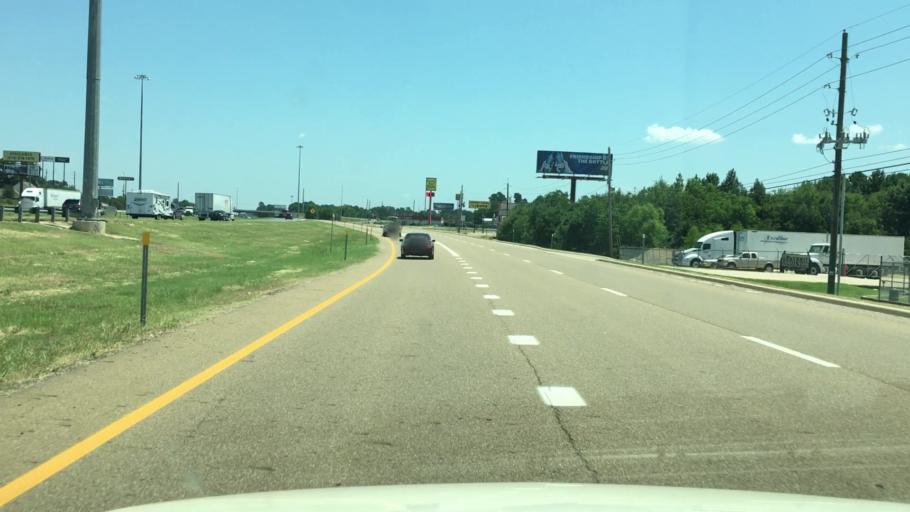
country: US
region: Arkansas
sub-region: Miller County
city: Texarkana
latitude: 33.4699
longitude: -94.0366
